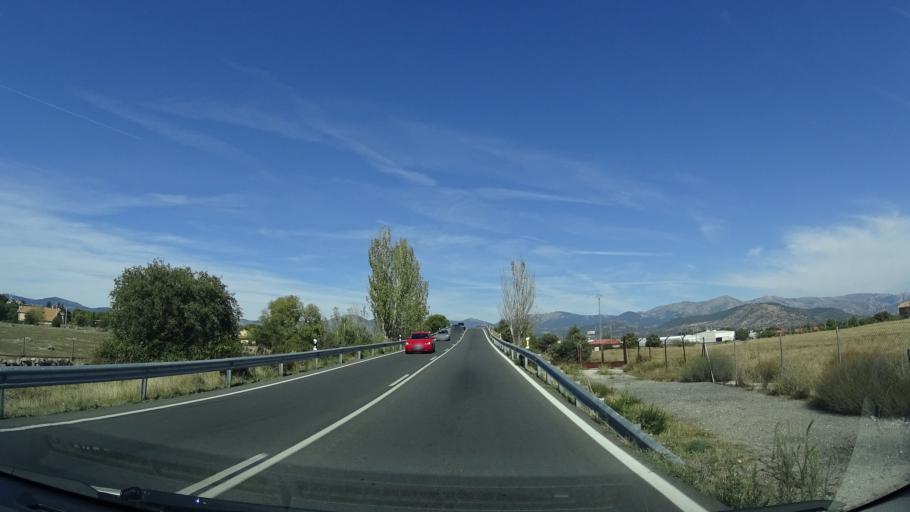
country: ES
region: Madrid
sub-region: Provincia de Madrid
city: Collado-Villalba
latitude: 40.6191
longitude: -4.0249
